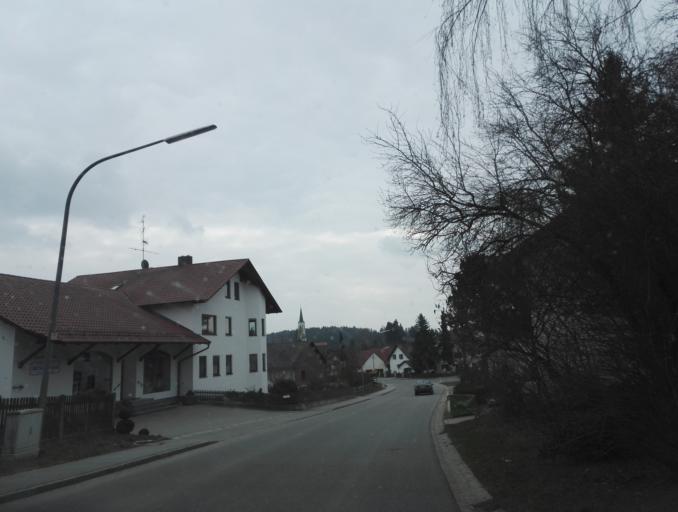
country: DE
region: Bavaria
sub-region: Lower Bavaria
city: Rottenburg an der Laaber
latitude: 48.6638
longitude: 12.0308
